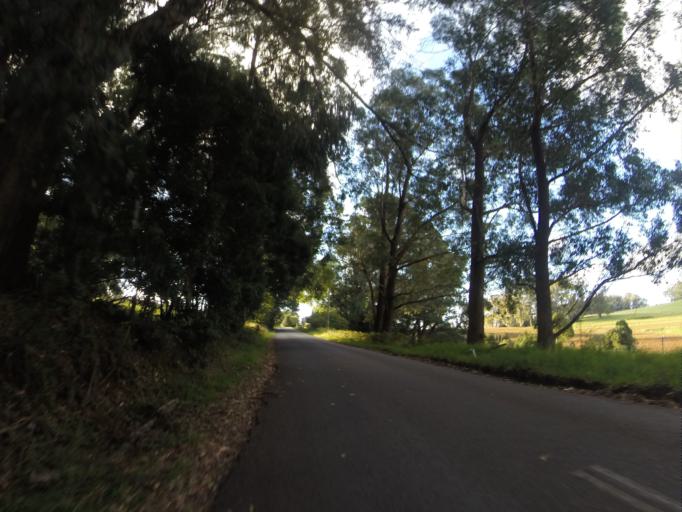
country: AU
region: New South Wales
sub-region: Shoalhaven Shire
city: Kangaroo Valley
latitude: -34.6129
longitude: 150.5351
